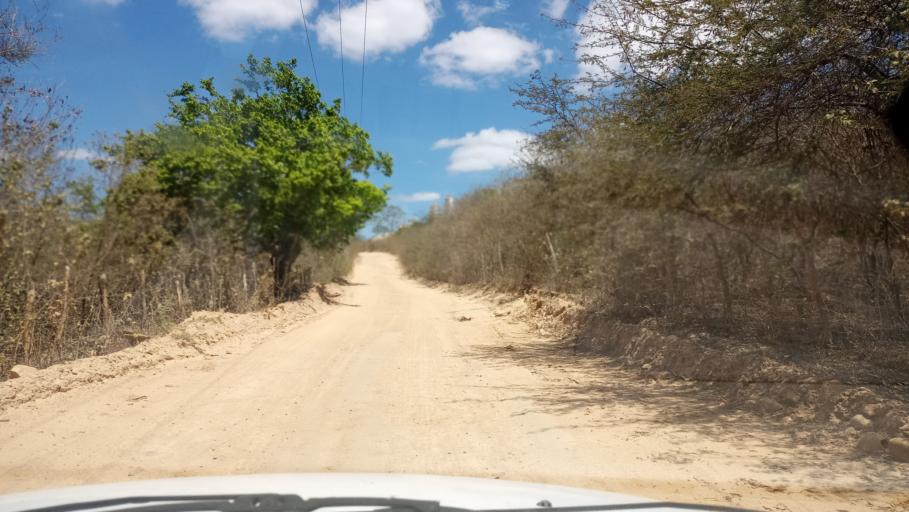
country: BR
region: Rio Grande do Norte
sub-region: Sao Paulo Do Potengi
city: Sao Paulo do Potengi
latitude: -5.7932
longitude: -35.9205
